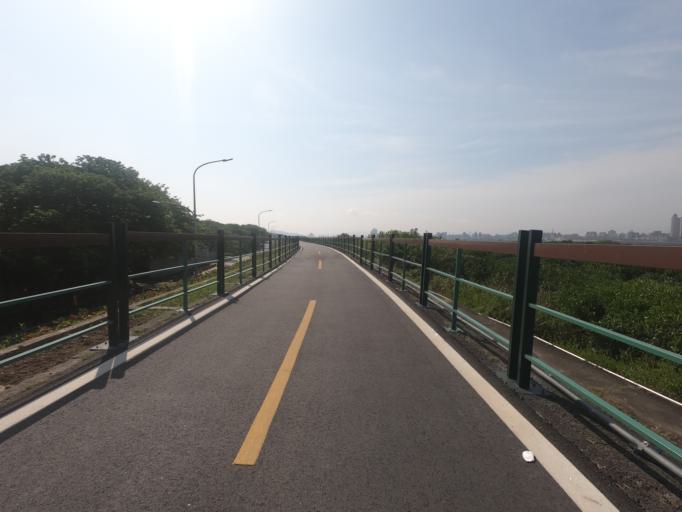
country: TW
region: Taipei
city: Taipei
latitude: 25.1089
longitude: 121.4665
